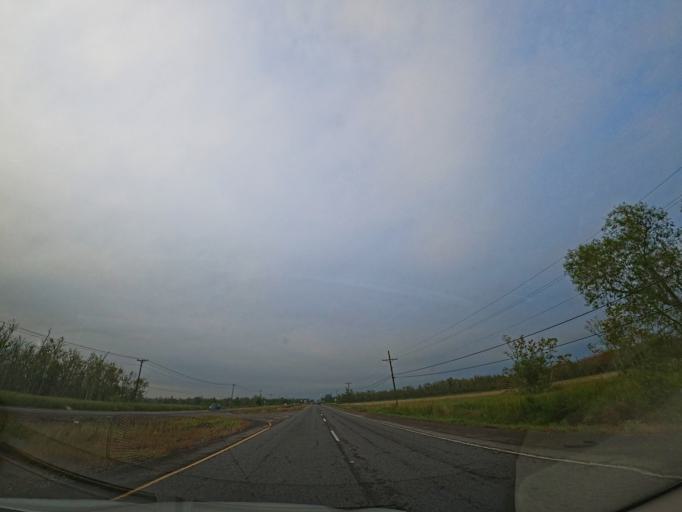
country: US
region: Louisiana
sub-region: Terrebonne Parish
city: Houma
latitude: 29.6594
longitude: -90.6755
